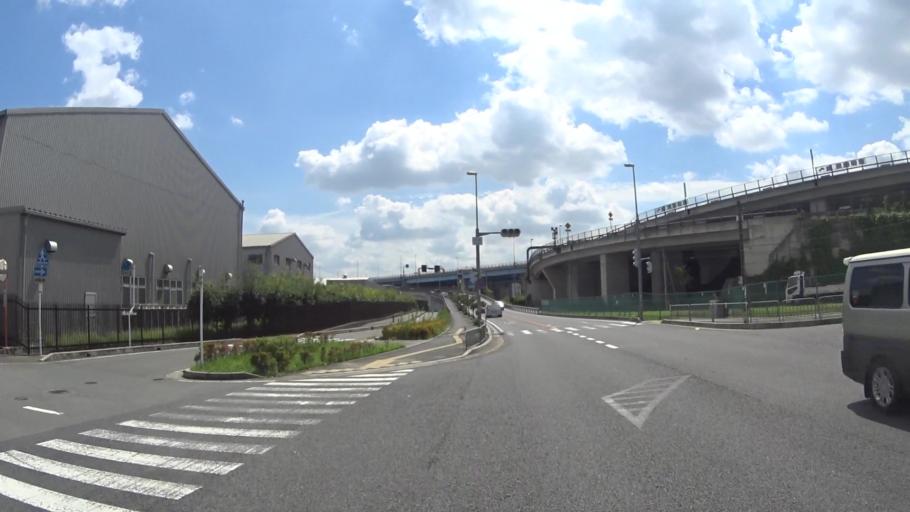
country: JP
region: Kyoto
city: Yawata
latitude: 34.9038
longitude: 135.6978
